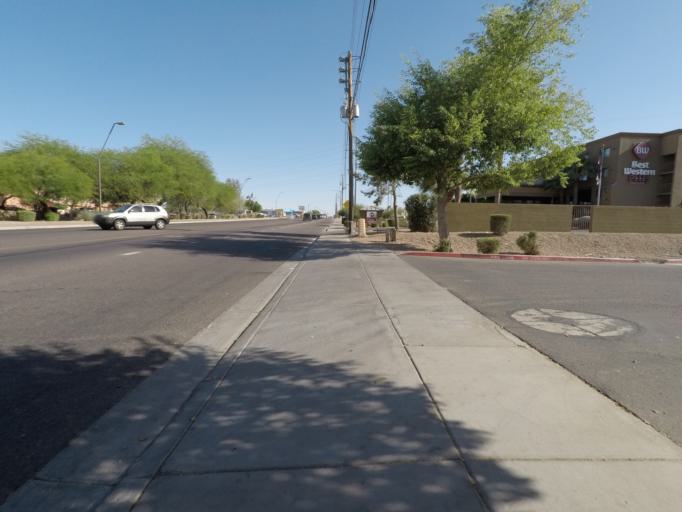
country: US
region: Arizona
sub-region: Maricopa County
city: Guadalupe
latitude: 33.3771
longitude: -111.9633
